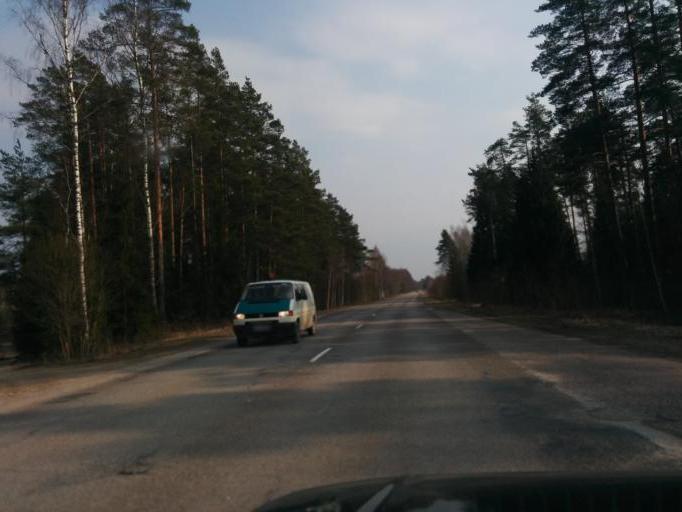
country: LV
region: Kekava
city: Balozi
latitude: 56.7827
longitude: 24.0940
